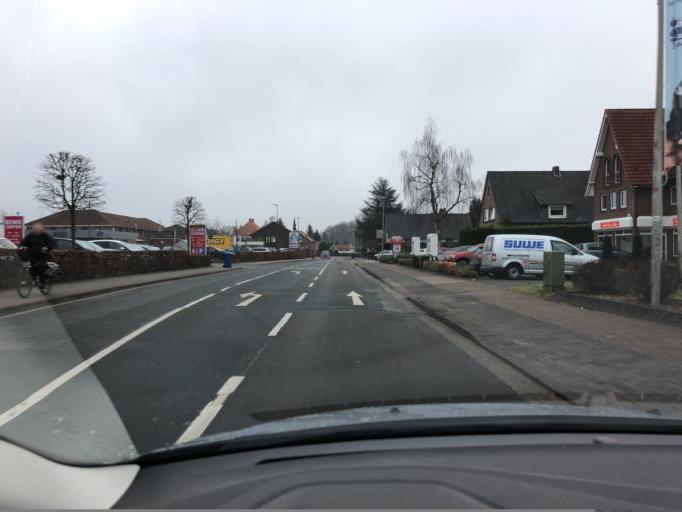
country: DE
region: Lower Saxony
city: Bad Zwischenahn
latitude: 53.1813
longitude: 8.0052
